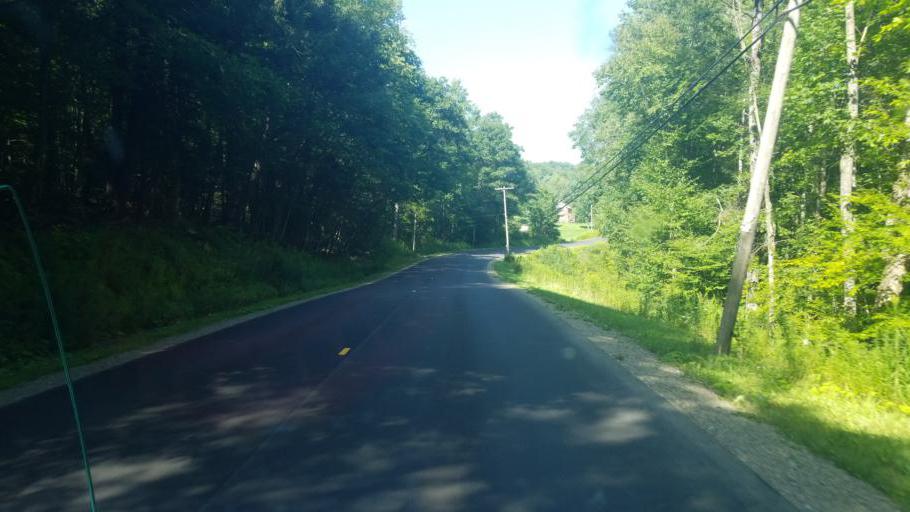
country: US
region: New York
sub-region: Allegany County
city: Wellsville
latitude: 42.0621
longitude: -78.0399
